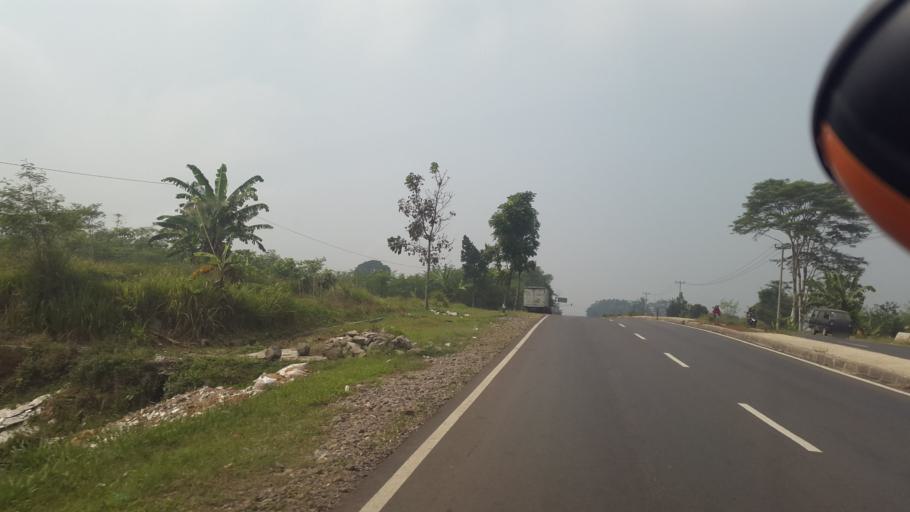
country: ID
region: West Java
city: Sukabumi
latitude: -6.9278
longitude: 106.8975
